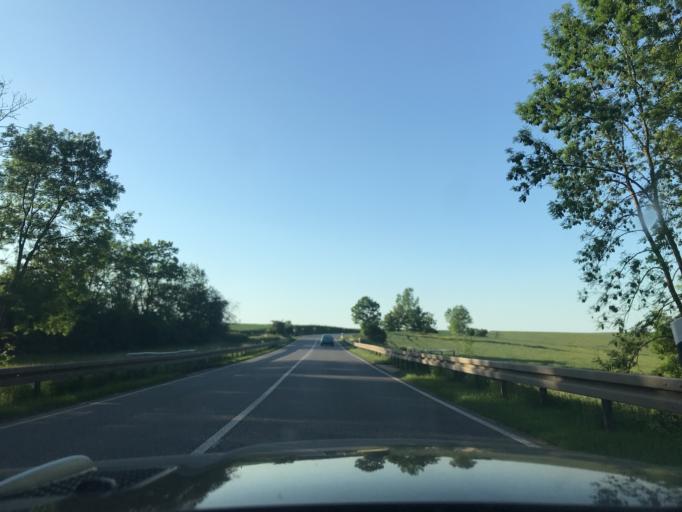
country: DE
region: Thuringia
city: Bad Langensalza
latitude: 51.0714
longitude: 10.6386
